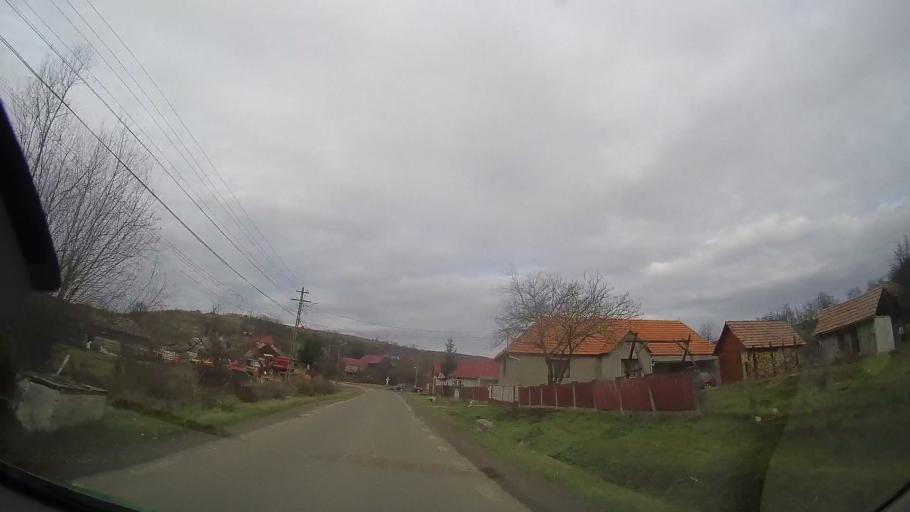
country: RO
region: Mures
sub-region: Comuna Cozma
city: Cozma
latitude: 46.8115
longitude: 24.5125
